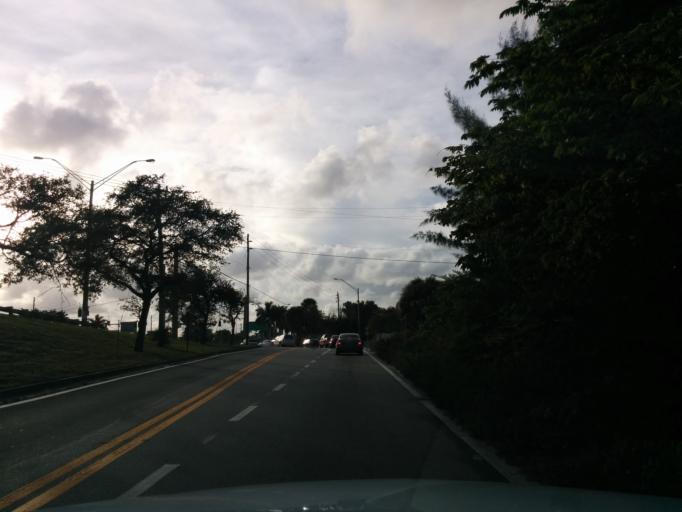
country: US
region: Florida
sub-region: Broward County
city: Dania Beach
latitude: 26.0632
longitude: -80.1599
